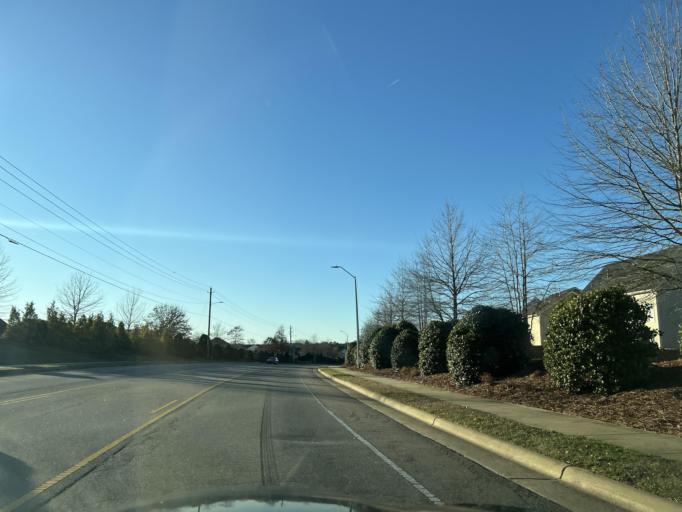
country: US
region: North Carolina
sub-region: Wake County
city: Fuquay-Varina
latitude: 35.5739
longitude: -78.8055
